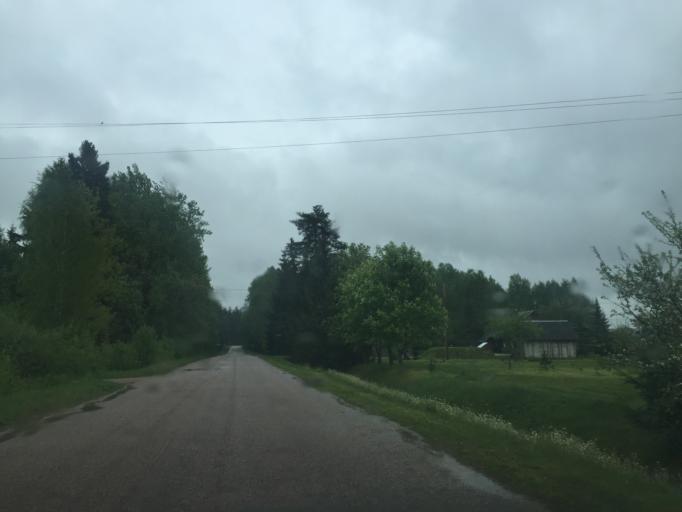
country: LV
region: Ogre
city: Jumprava
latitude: 56.6786
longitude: 24.9783
